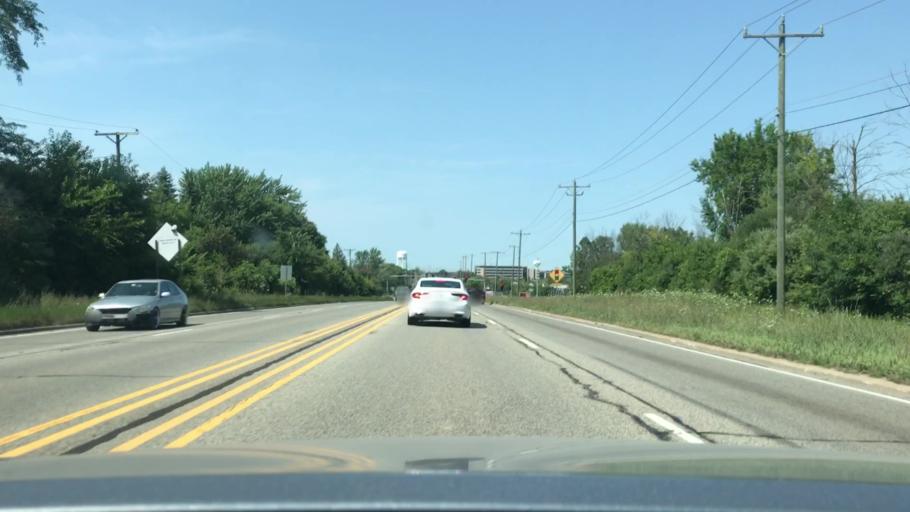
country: US
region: Illinois
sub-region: Kane County
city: Batavia
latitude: 41.8516
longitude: -88.2787
